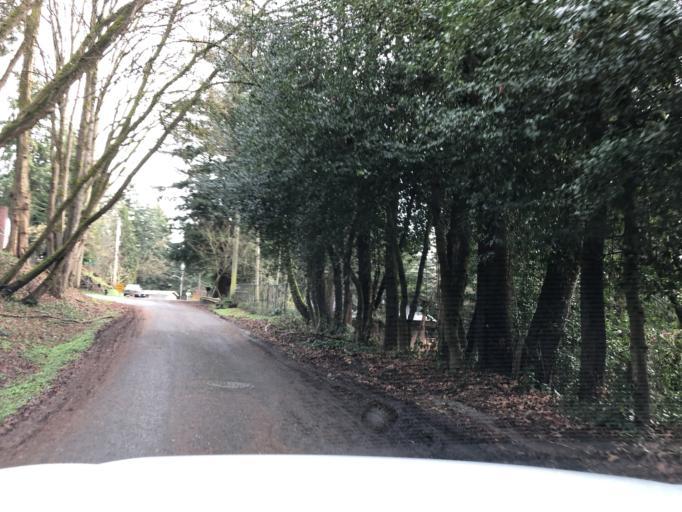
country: US
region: Washington
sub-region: King County
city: Lake Forest Park
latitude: 47.7141
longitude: -122.2948
